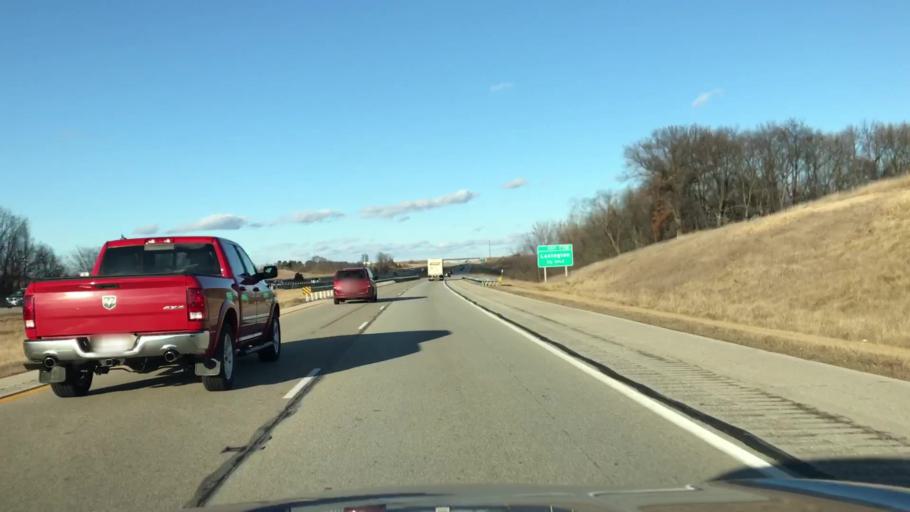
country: US
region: Illinois
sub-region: McLean County
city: Lexington
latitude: 40.6338
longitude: -88.8147
